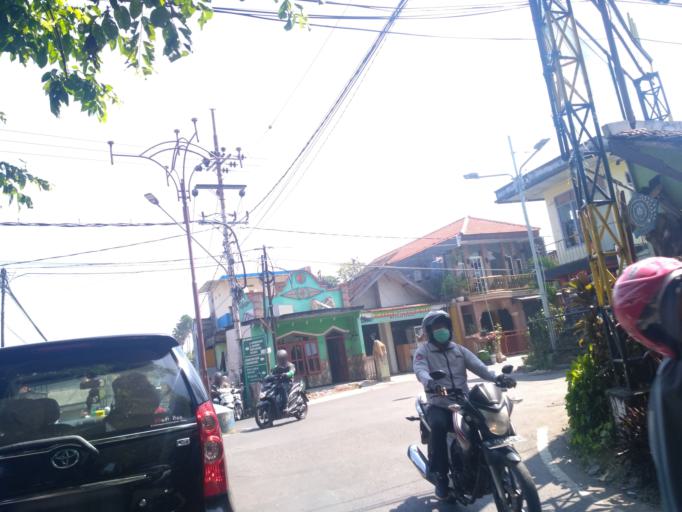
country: ID
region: East Java
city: Malang
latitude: -7.9331
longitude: 112.6134
